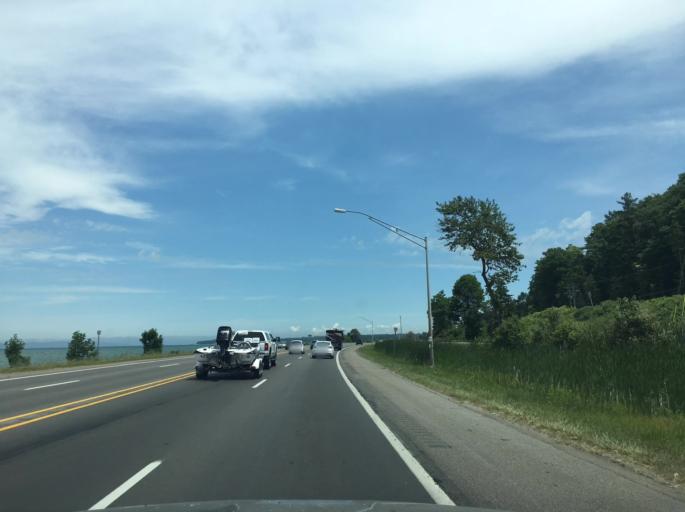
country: US
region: Michigan
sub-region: Grand Traverse County
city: Traverse City
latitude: 44.7534
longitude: -85.5217
